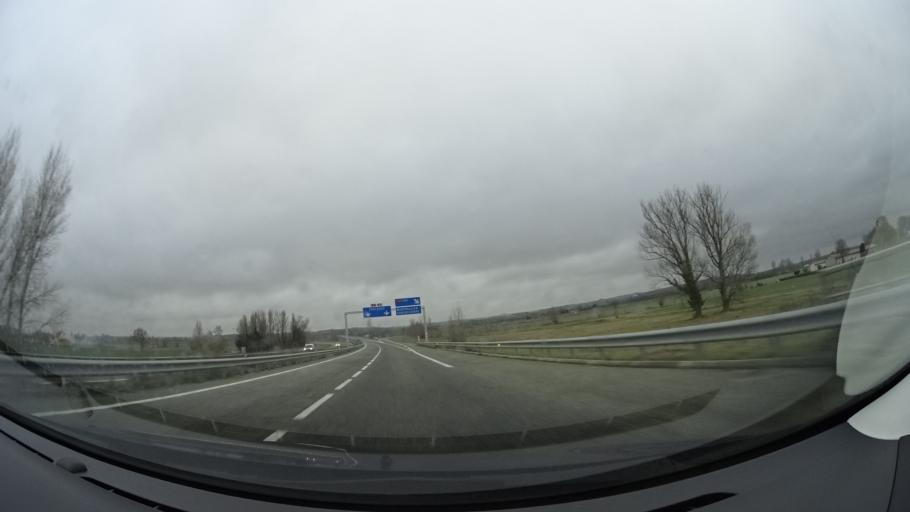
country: FR
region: Midi-Pyrenees
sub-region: Departement de la Haute-Garonne
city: Villenouvelle
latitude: 43.4122
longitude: 1.6522
